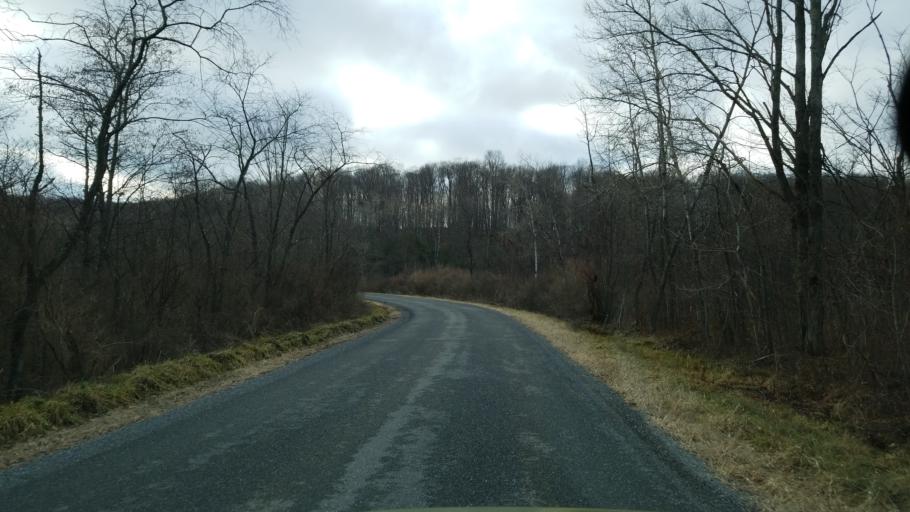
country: US
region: Pennsylvania
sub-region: Clearfield County
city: Treasure Lake
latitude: 41.1401
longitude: -78.5989
